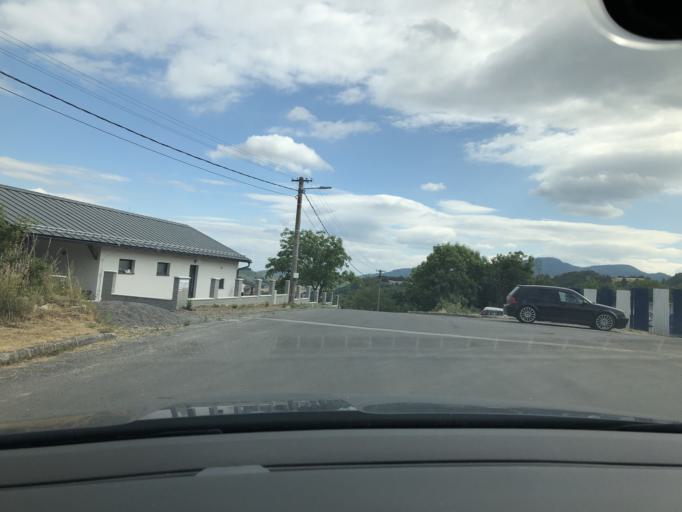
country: SK
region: Banskobystricky
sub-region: Okres Banska Bystrica
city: Banska Stiavnica
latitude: 48.4577
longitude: 18.9069
